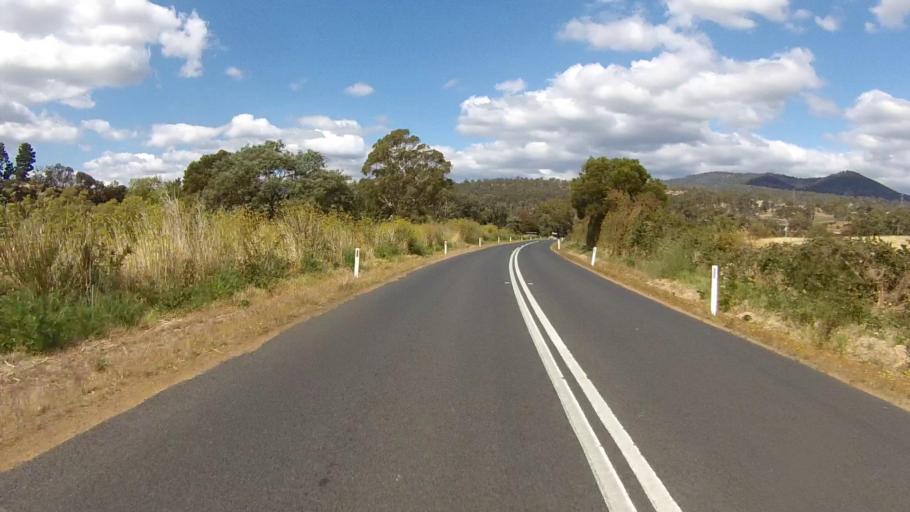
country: AU
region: Tasmania
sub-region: Derwent Valley
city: New Norfolk
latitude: -42.7699
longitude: 147.0261
